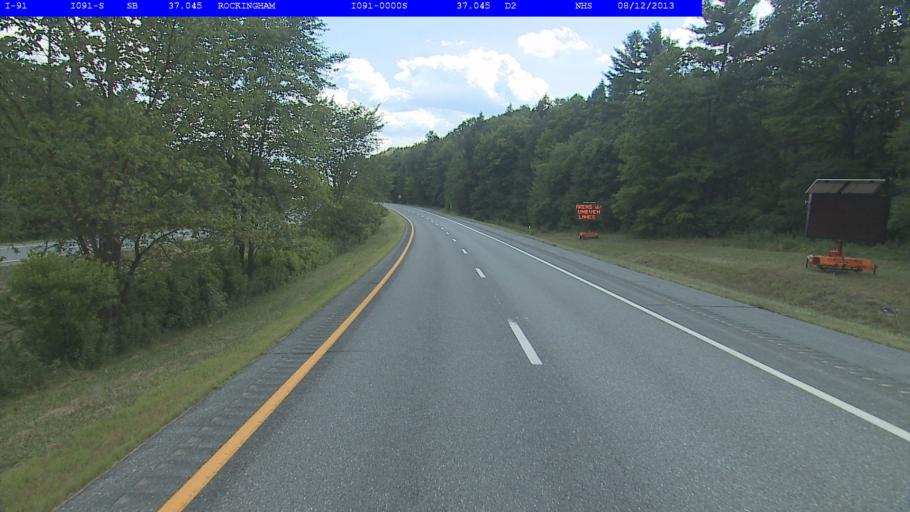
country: US
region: Vermont
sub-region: Windham County
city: Rockingham
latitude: 43.2046
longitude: -72.4567
